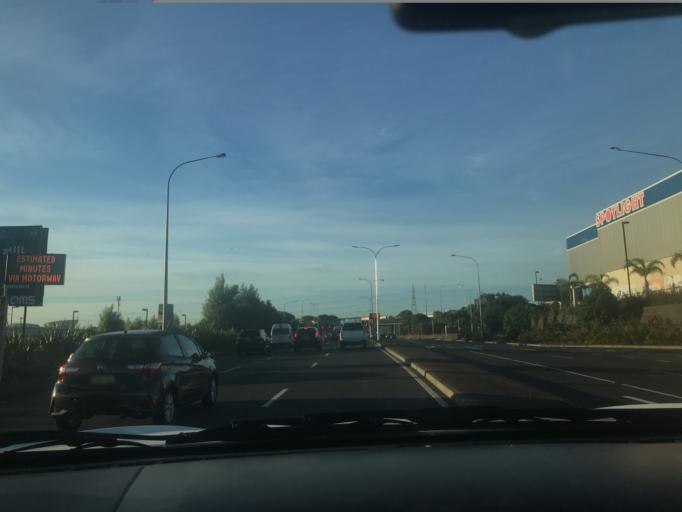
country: NZ
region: Auckland
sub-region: Auckland
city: Tamaki
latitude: -36.9166
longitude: 174.8394
